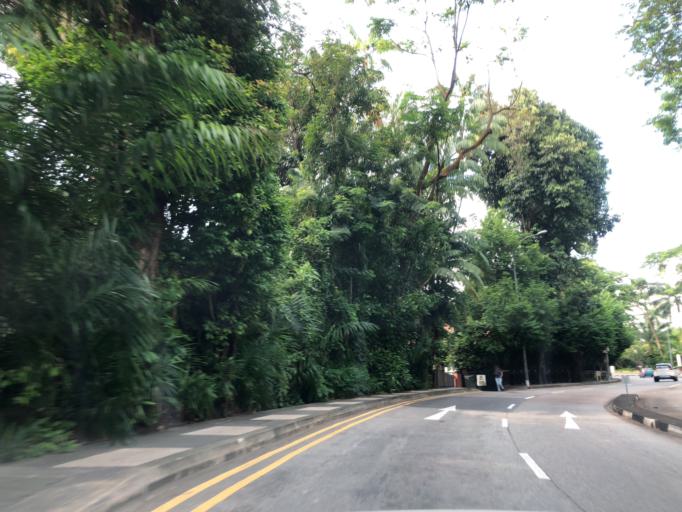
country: SG
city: Singapore
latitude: 1.3094
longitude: 103.8260
